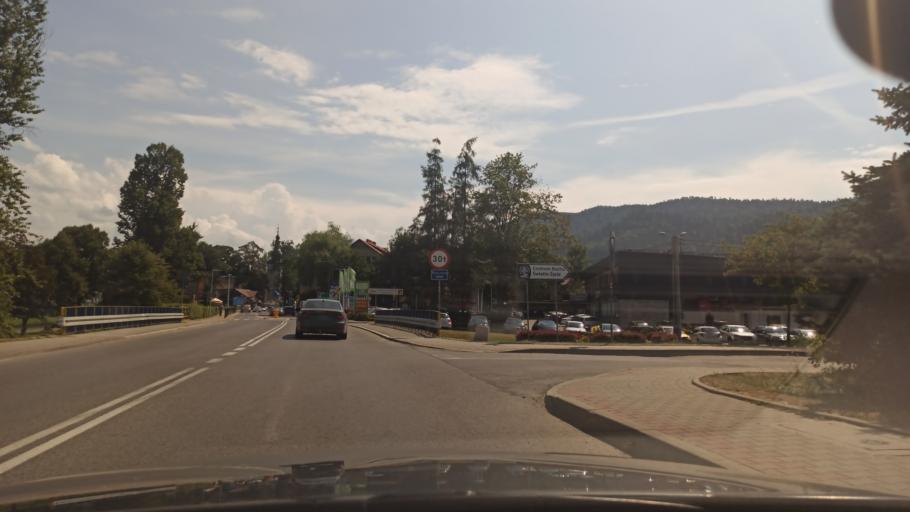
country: PL
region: Lesser Poland Voivodeship
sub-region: Powiat nowotarski
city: Kroscienko nad Dunajcem
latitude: 49.4428
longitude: 20.4271
